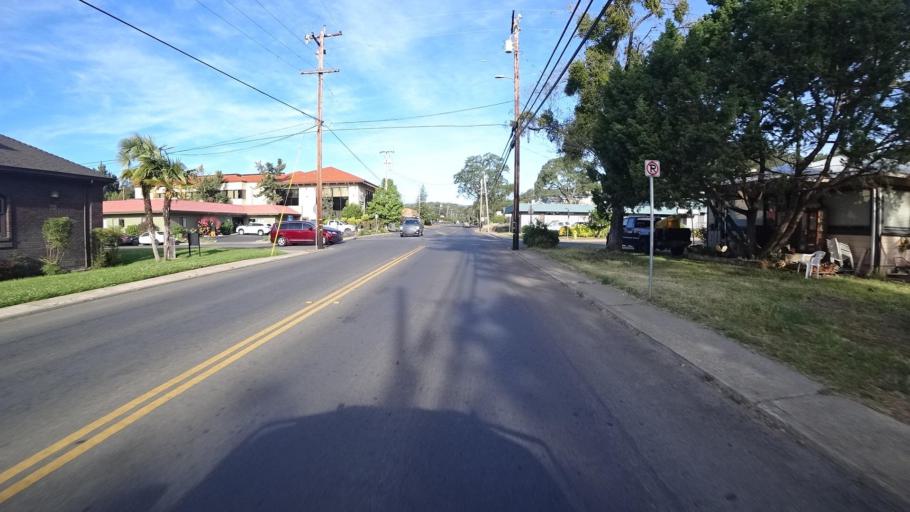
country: US
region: California
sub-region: Lake County
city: Lakeport
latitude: 39.0490
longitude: -122.9212
